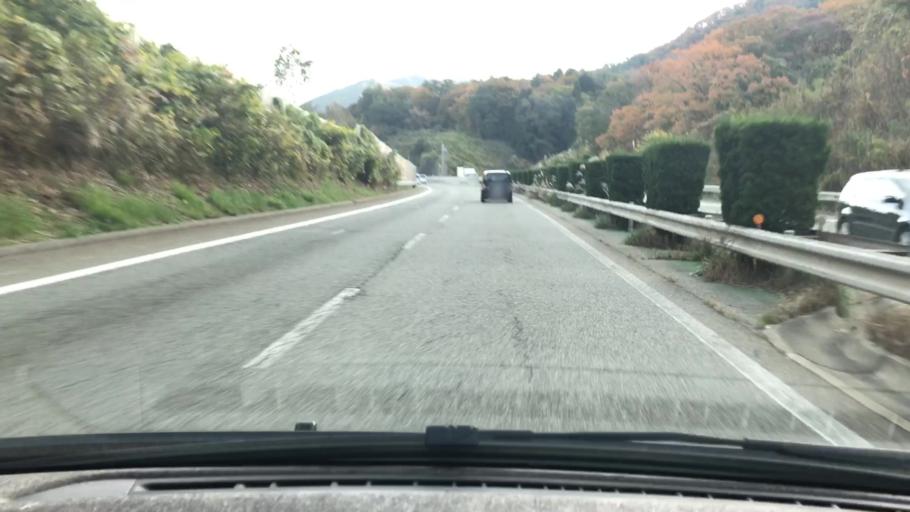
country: JP
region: Hyogo
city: Kobe
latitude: 34.7632
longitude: 135.1909
